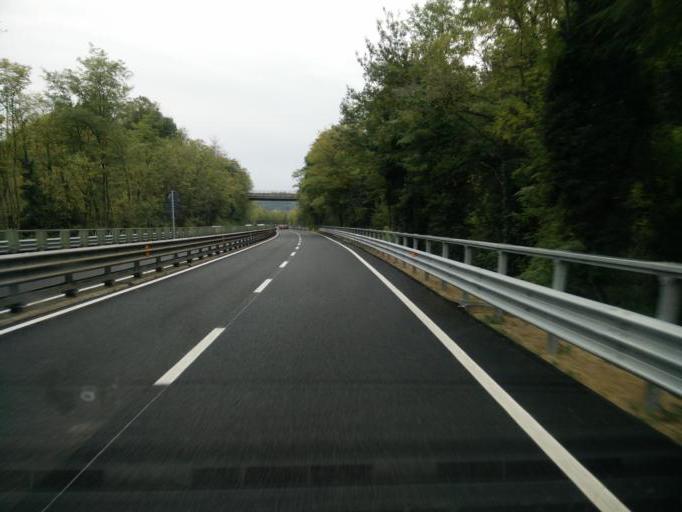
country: IT
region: Tuscany
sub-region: Provincia di Siena
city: Bellavista
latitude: 43.4489
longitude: 11.1531
